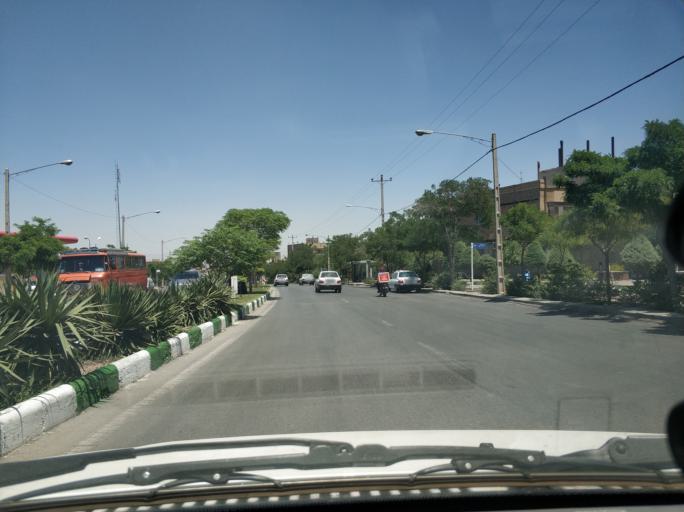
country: IR
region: Razavi Khorasan
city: Mashhad
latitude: 36.2963
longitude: 59.5071
